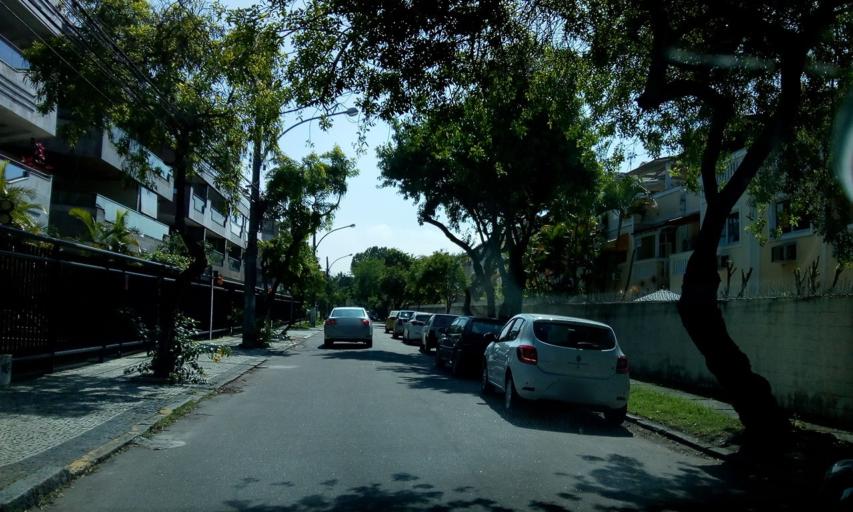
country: BR
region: Rio de Janeiro
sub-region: Nilopolis
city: Nilopolis
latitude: -23.0139
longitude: -43.4575
